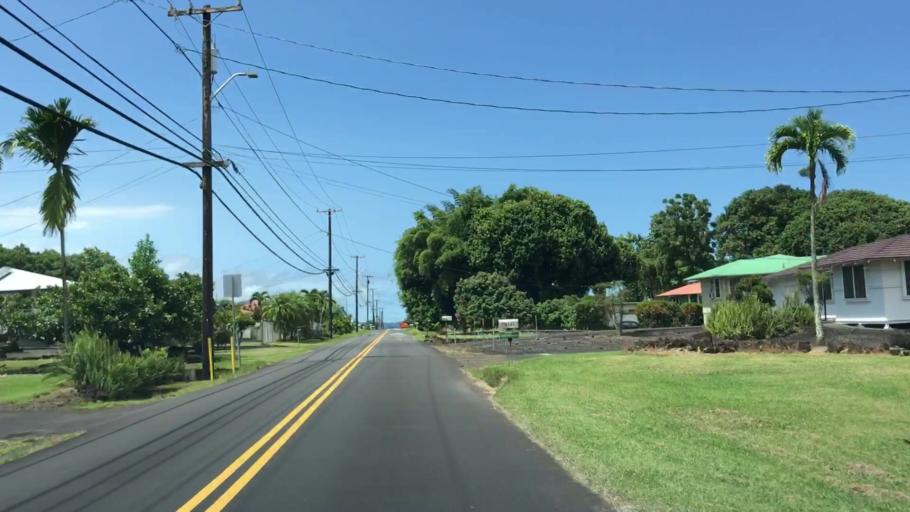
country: US
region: Hawaii
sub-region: Hawaii County
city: Hilo
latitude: 19.6791
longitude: -155.0801
